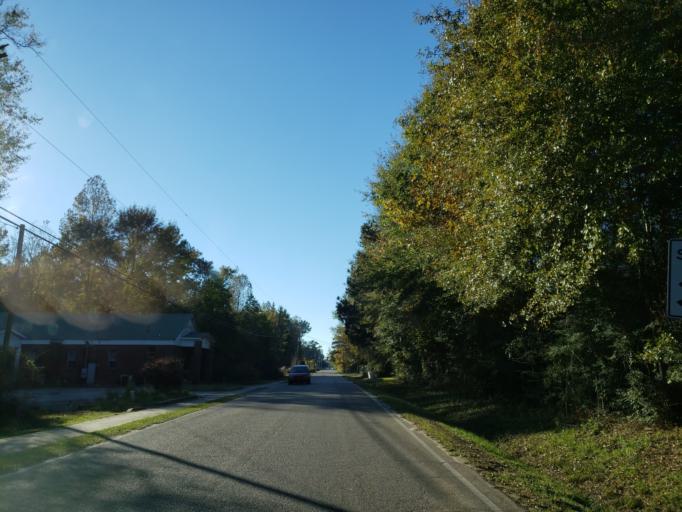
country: US
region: Mississippi
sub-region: Forrest County
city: Hattiesburg
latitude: 31.2774
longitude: -89.2758
